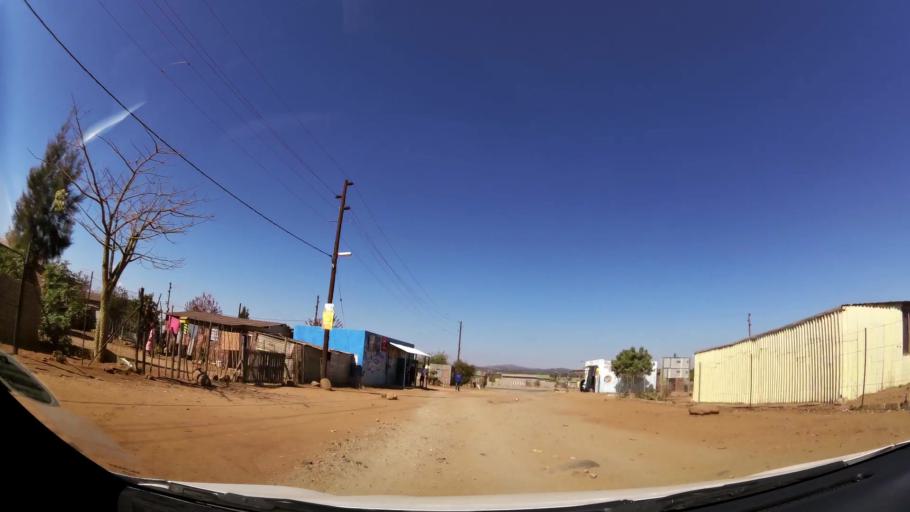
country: ZA
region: Limpopo
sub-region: Capricorn District Municipality
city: Polokwane
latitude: -23.8942
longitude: 29.4149
